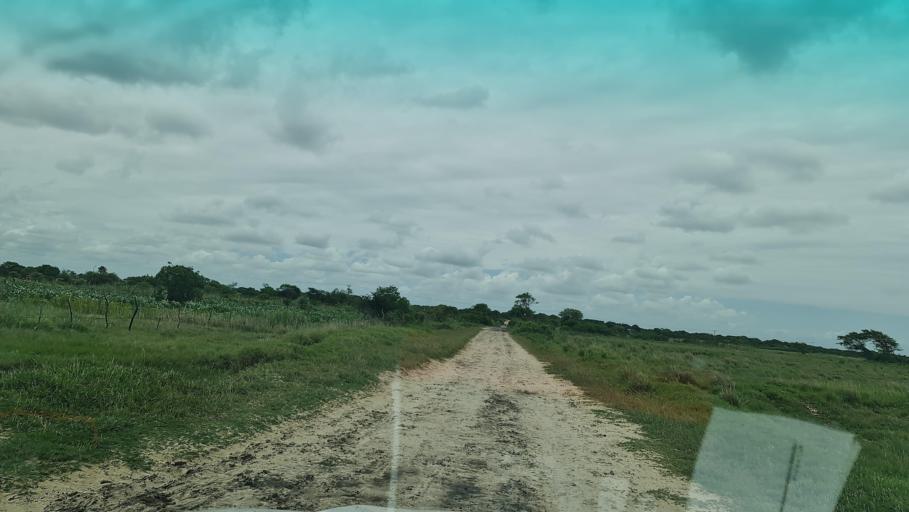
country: MZ
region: Maputo City
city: Maputo
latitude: -25.7030
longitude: 32.7043
